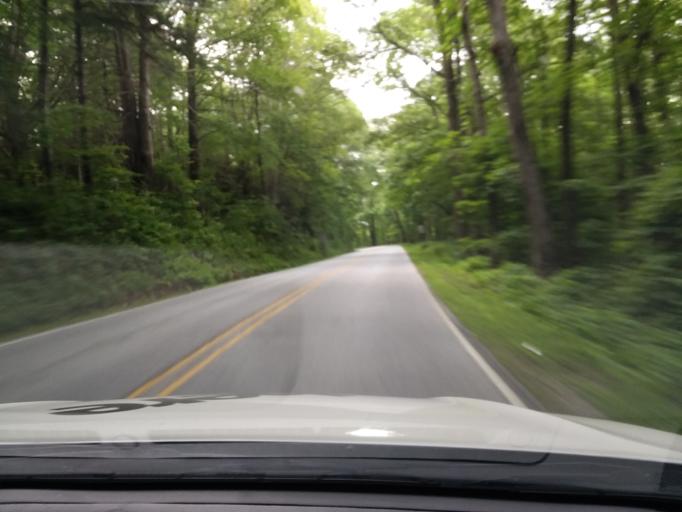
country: US
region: Georgia
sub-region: Rabun County
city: Mountain City
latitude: 35.0399
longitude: -83.2466
